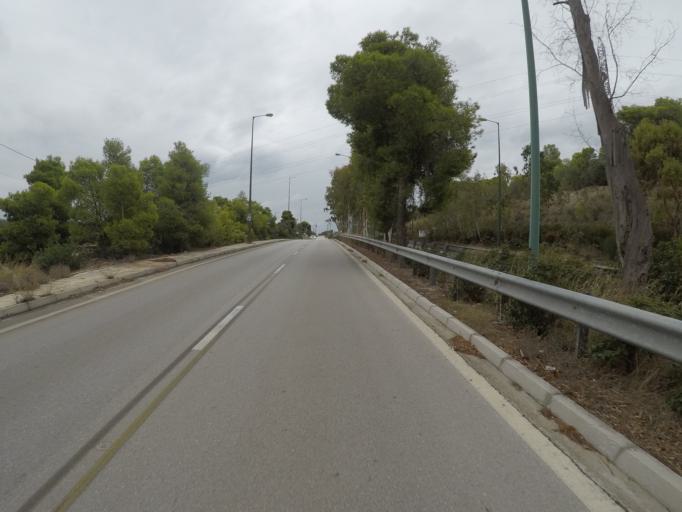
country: GR
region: Peloponnese
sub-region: Nomos Korinthias
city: Kyras Vrysi
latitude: 37.9334
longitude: 22.9899
